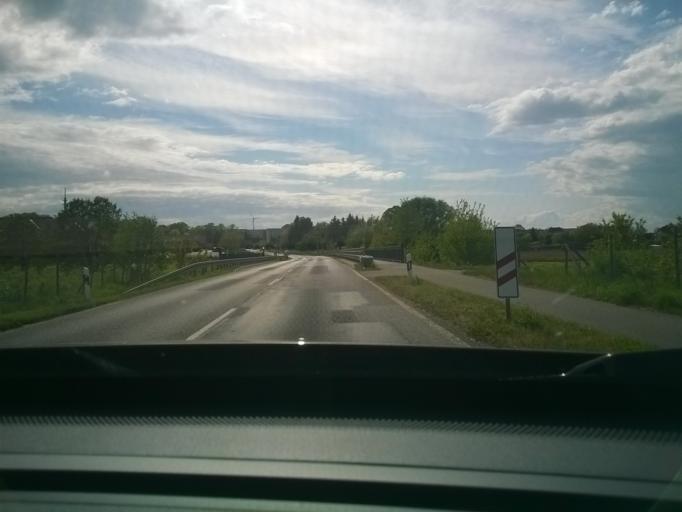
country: DE
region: Brandenburg
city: Wittstock
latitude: 53.1547
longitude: 12.4909
